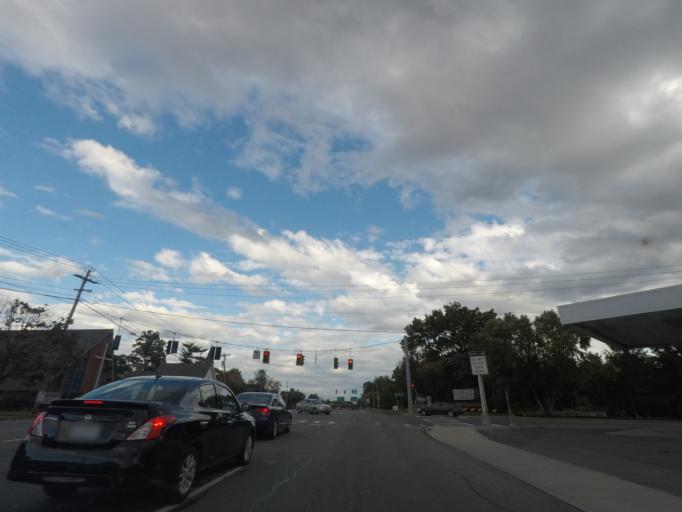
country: US
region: New York
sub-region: Albany County
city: McKownville
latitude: 42.6842
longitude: -73.8478
